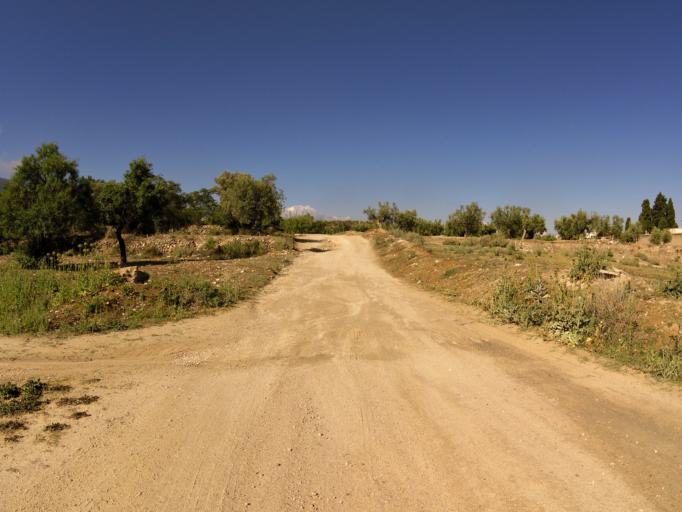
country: ES
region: Valencia
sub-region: Provincia de Alicante
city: Biar
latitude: 38.6385
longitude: -0.7720
